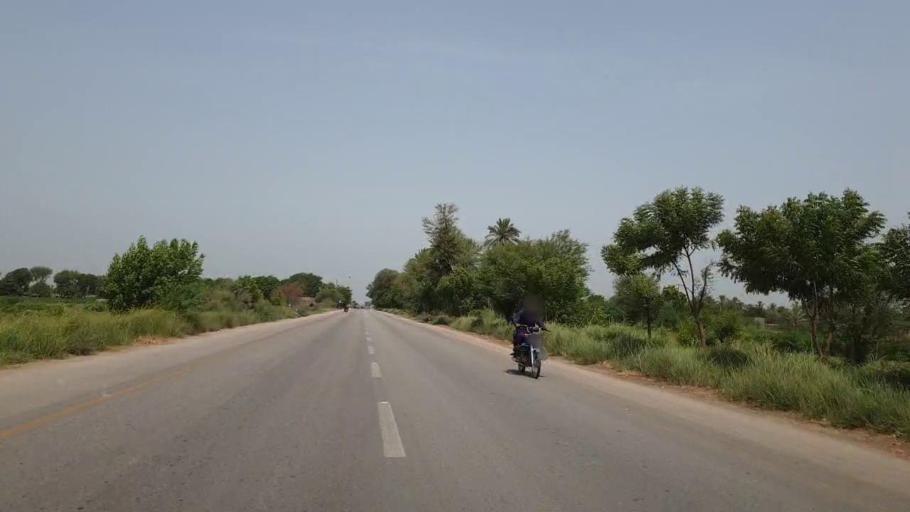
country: PK
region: Sindh
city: Nawabshah
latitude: 26.2200
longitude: 68.5009
